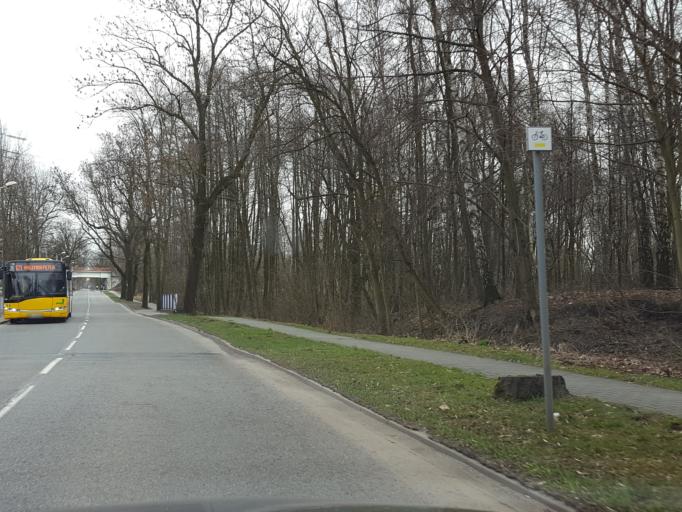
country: PL
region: Silesian Voivodeship
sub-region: Ruda Slaska
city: Ruda Slaska
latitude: 50.2372
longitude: 18.8432
